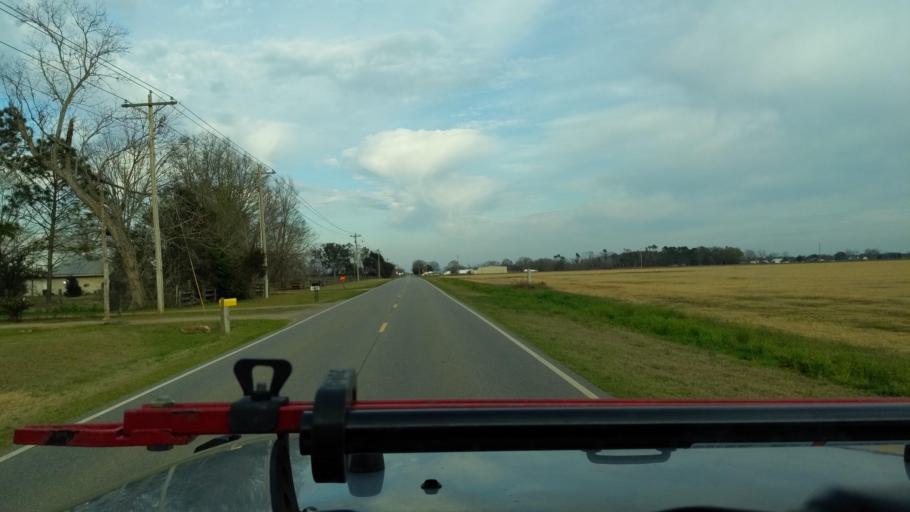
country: US
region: Alabama
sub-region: Baldwin County
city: Foley
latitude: 30.4579
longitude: -87.7209
